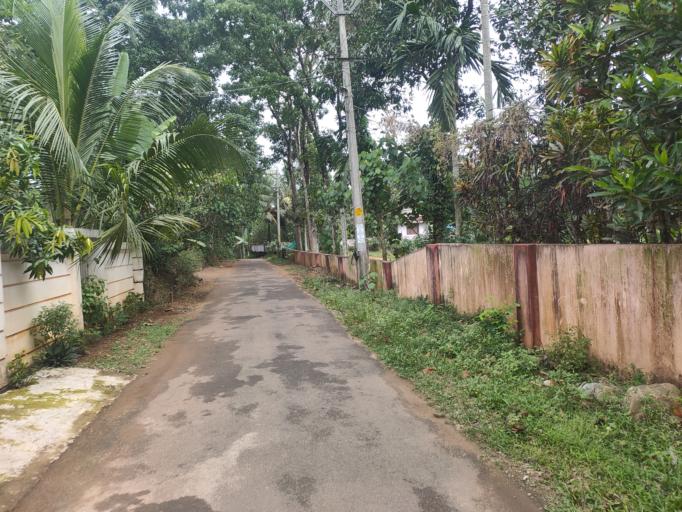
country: IN
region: Kerala
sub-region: Ernakulam
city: Kotamangalam
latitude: 10.0057
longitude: 76.6449
